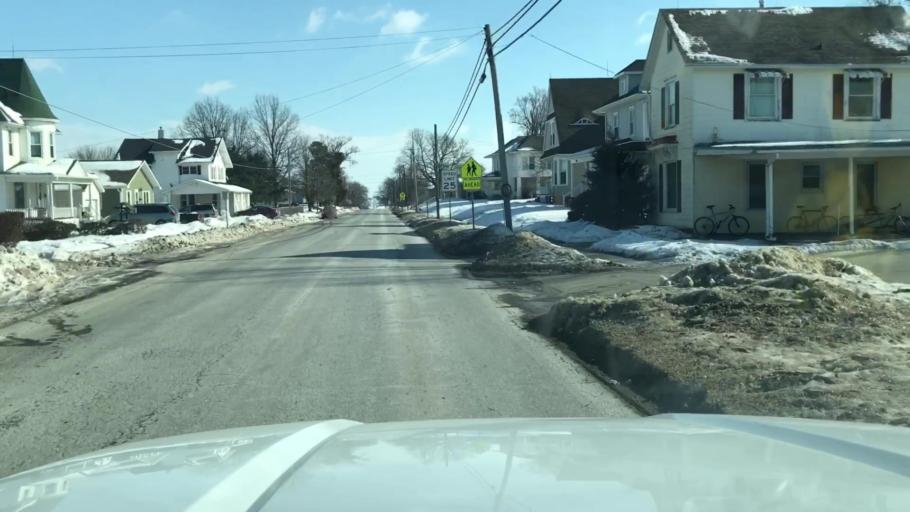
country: US
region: Missouri
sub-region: Nodaway County
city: Maryville
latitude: 40.3455
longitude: -94.8692
